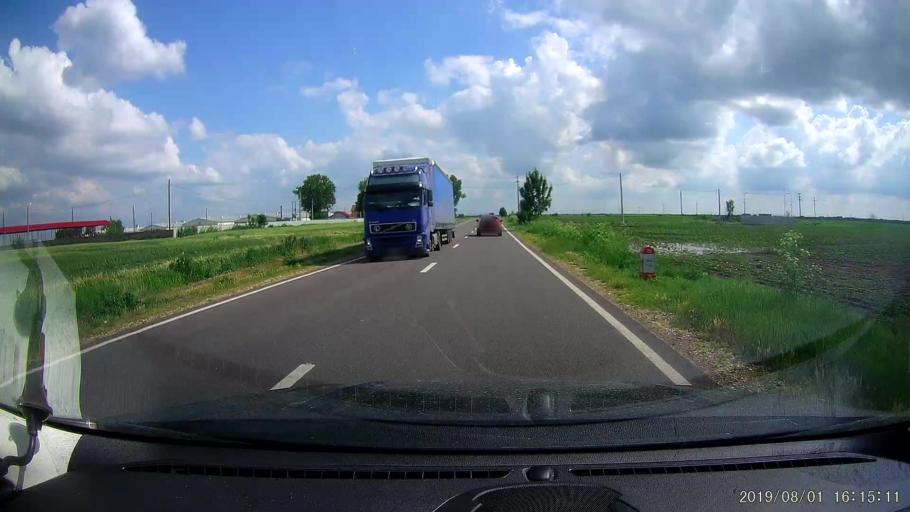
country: RO
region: Calarasi
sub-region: Comuna Stefan Voda
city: Stefan Voda
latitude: 44.3422
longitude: 27.3618
